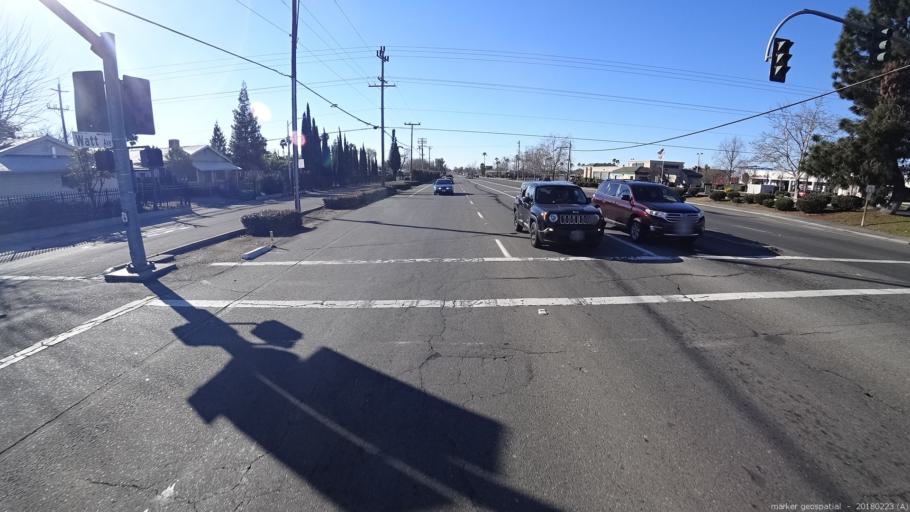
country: US
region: California
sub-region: Sacramento County
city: North Highlands
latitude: 38.6978
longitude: -121.3828
